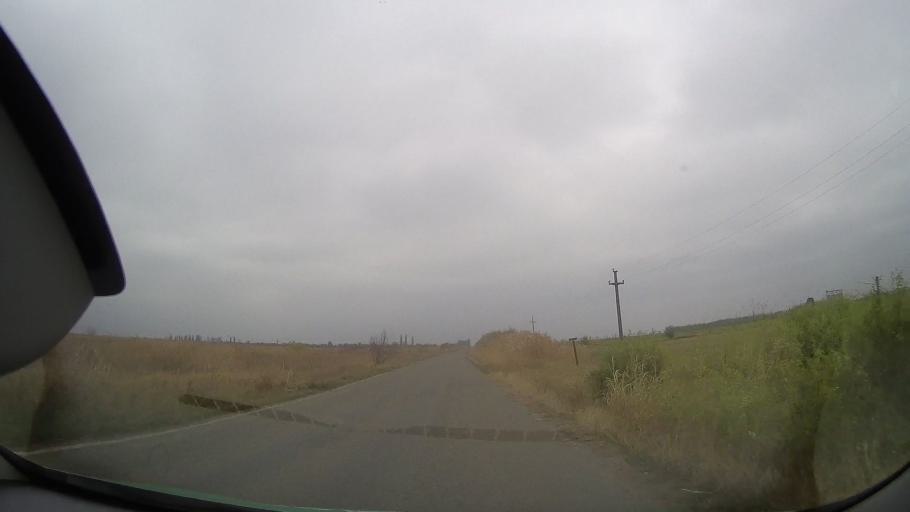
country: RO
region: Buzau
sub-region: Comuna Glodeanu-Silistea
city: Glodeanu-Silistea
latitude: 44.8156
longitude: 26.8452
